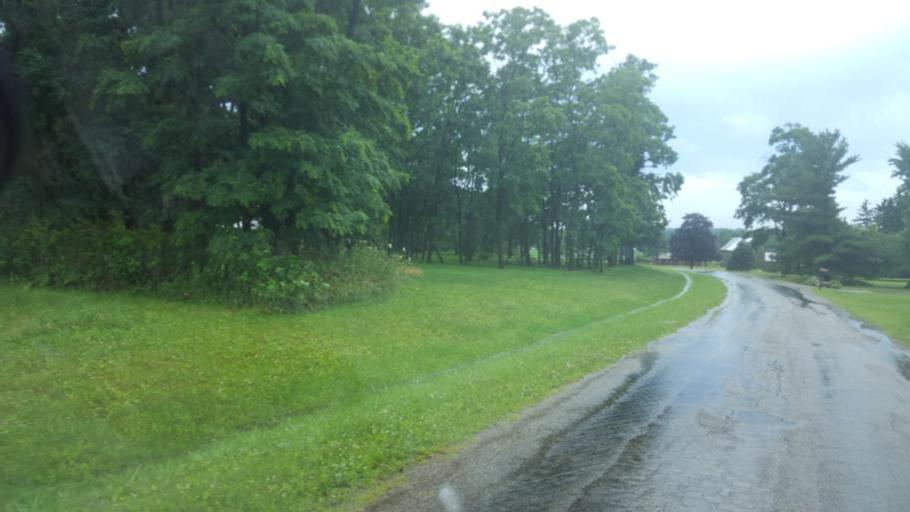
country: US
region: Ohio
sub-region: Richland County
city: Lexington
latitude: 40.6716
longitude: -82.6383
